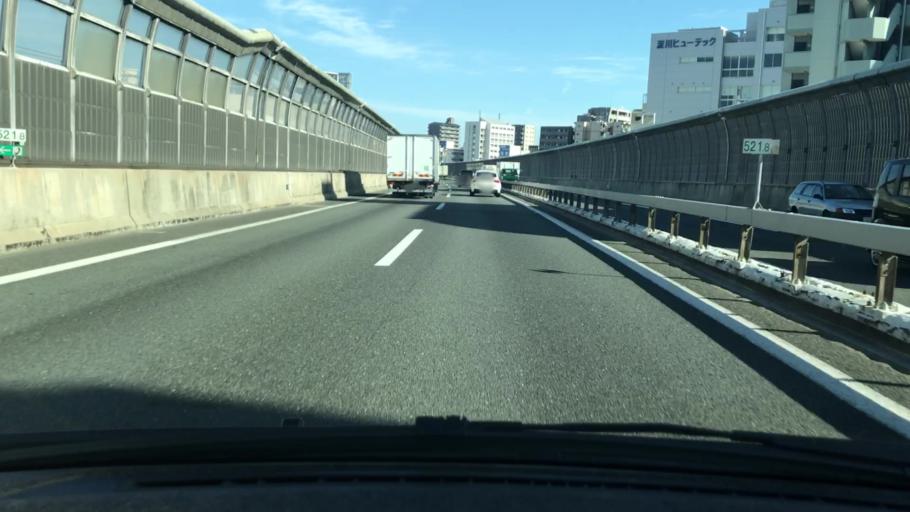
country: JP
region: Osaka
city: Suita
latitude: 34.7624
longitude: 135.4927
